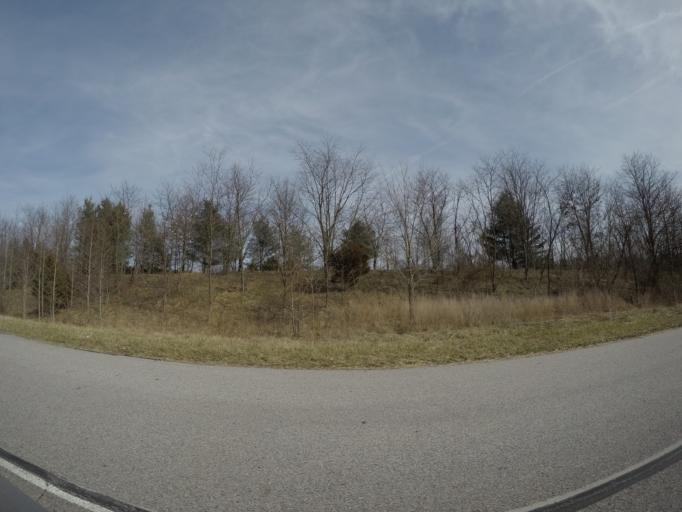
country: US
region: Maryland
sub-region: Cecil County
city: Perryville
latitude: 39.5663
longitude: -76.0612
